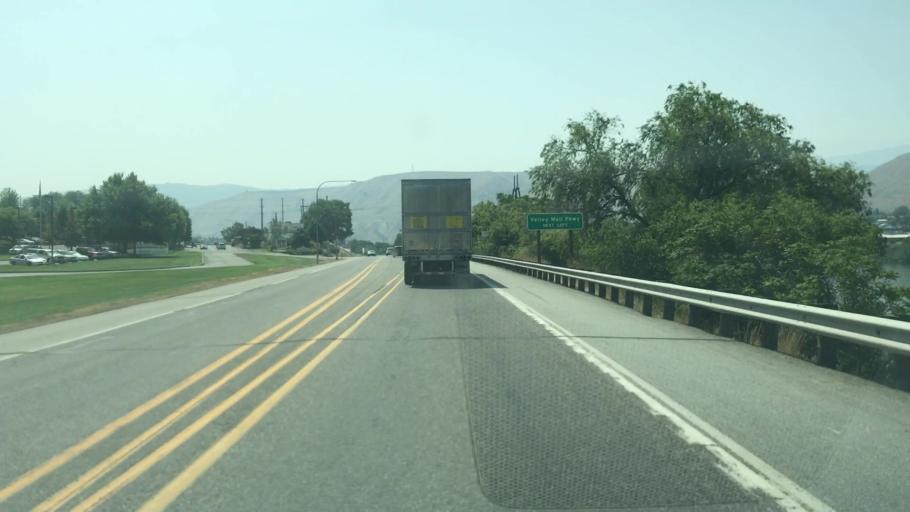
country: US
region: Washington
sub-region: Douglas County
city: East Wenatchee
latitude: 47.4224
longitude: -120.2974
